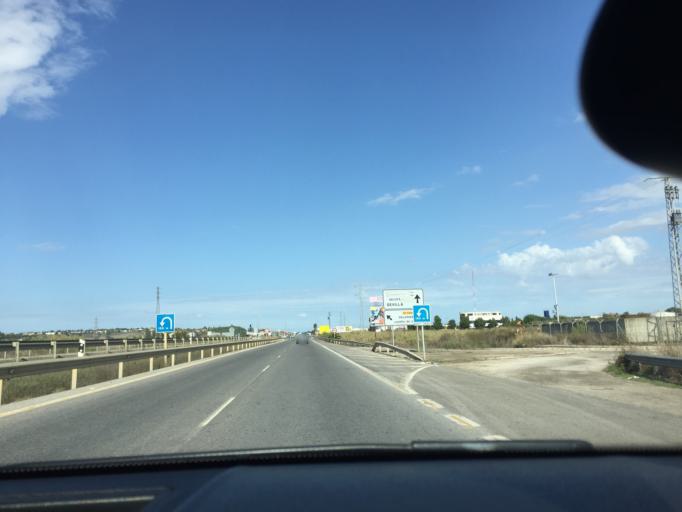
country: ES
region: Andalusia
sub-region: Provincia de Sevilla
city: Palomares del Rio
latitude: 37.3088
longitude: -6.0384
